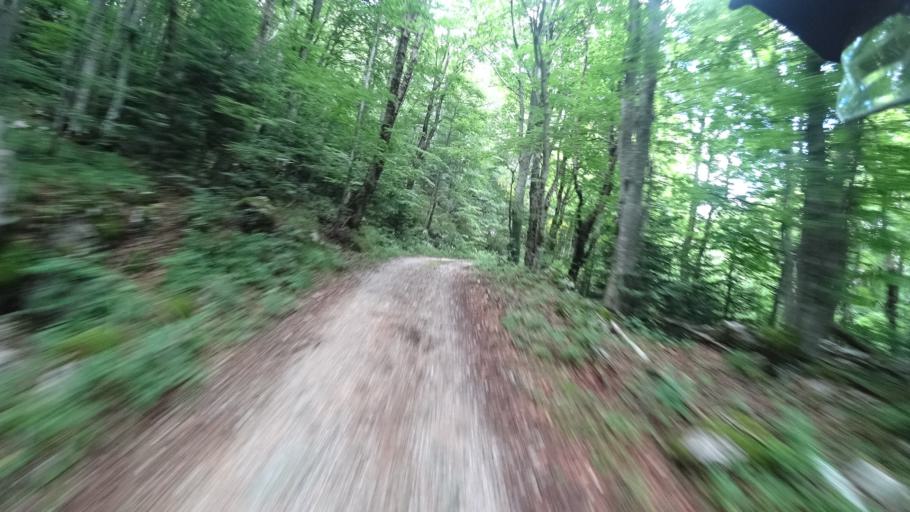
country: HR
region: Primorsko-Goranska
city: Bribir
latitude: 45.2351
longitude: 14.7613
